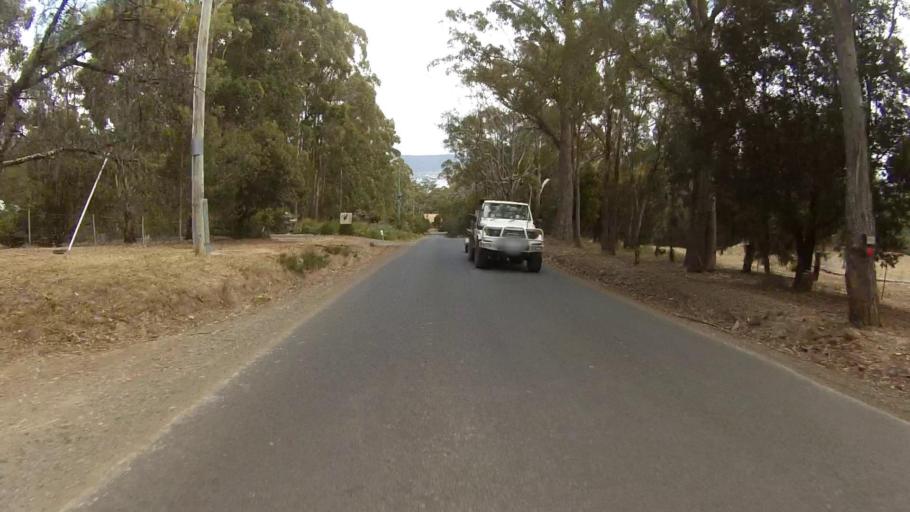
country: AU
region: Tasmania
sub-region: Kingborough
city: Blackmans Bay
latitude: -43.0325
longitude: 147.3091
